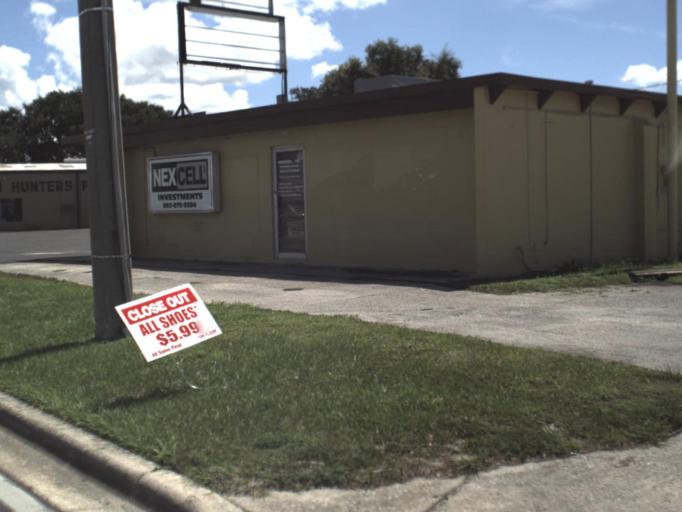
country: US
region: Florida
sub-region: Polk County
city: Inwood
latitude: 28.0477
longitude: -81.7635
